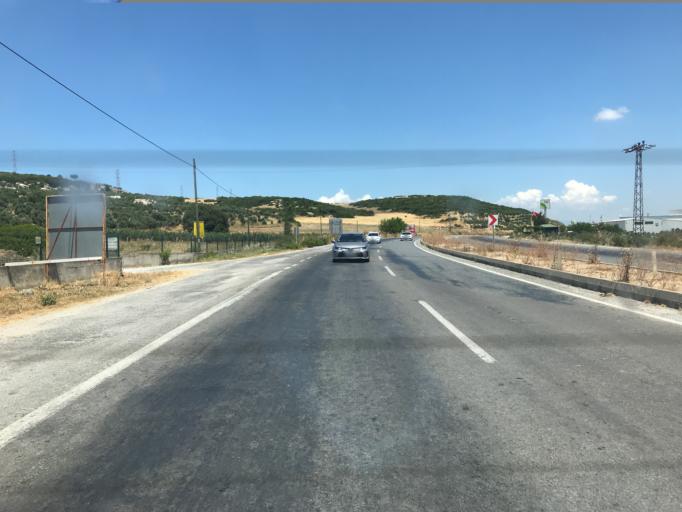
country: TR
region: Aydin
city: Akkoy
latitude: 37.4816
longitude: 27.3386
